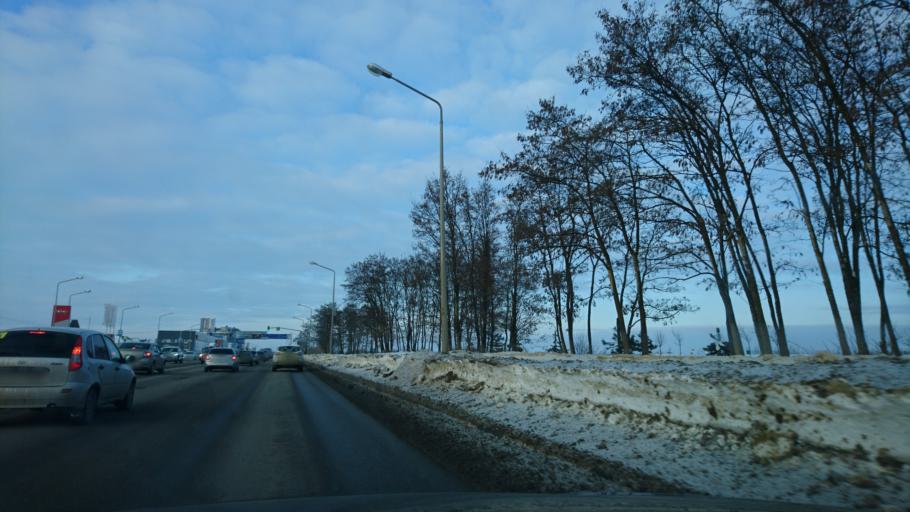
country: RU
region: Belgorod
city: Severnyy
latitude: 50.6507
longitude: 36.5667
